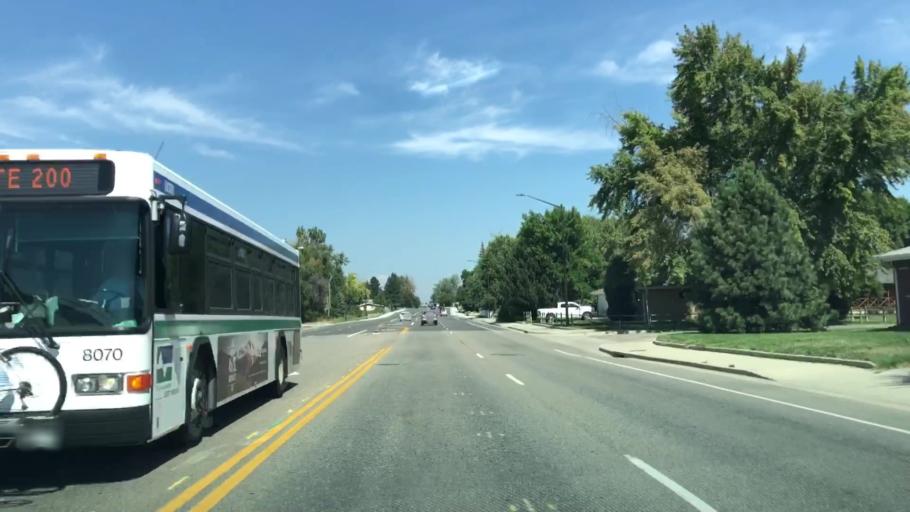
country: US
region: Colorado
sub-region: Larimer County
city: Loveland
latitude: 40.4005
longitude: -105.0970
